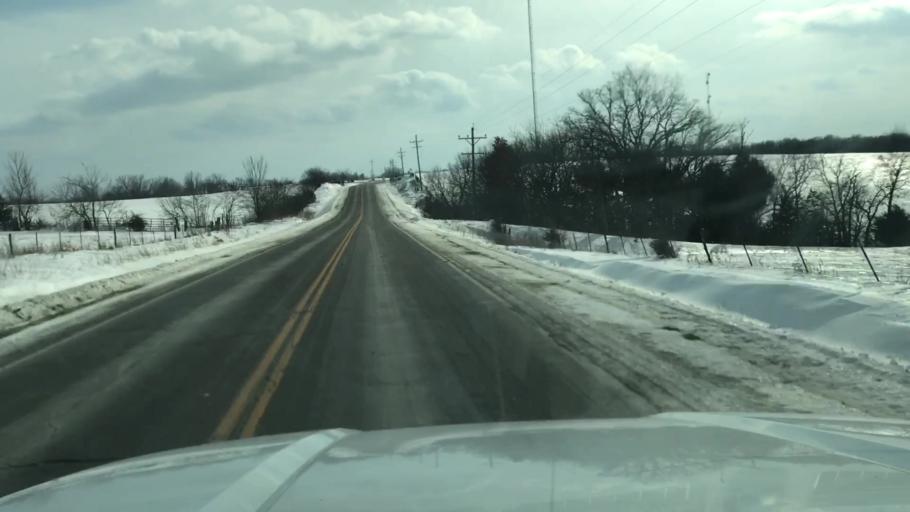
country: US
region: Missouri
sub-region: Gentry County
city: Stanberry
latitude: 40.3733
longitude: -94.6473
